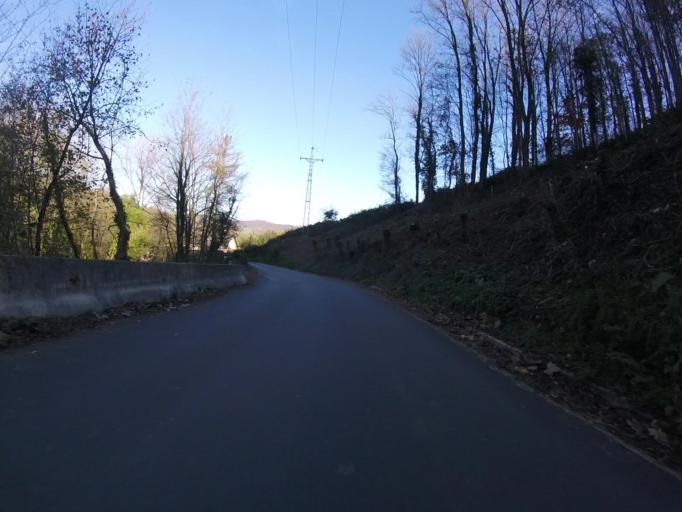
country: ES
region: Navarre
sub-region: Provincia de Navarra
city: Igantzi
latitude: 43.2342
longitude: -1.7016
